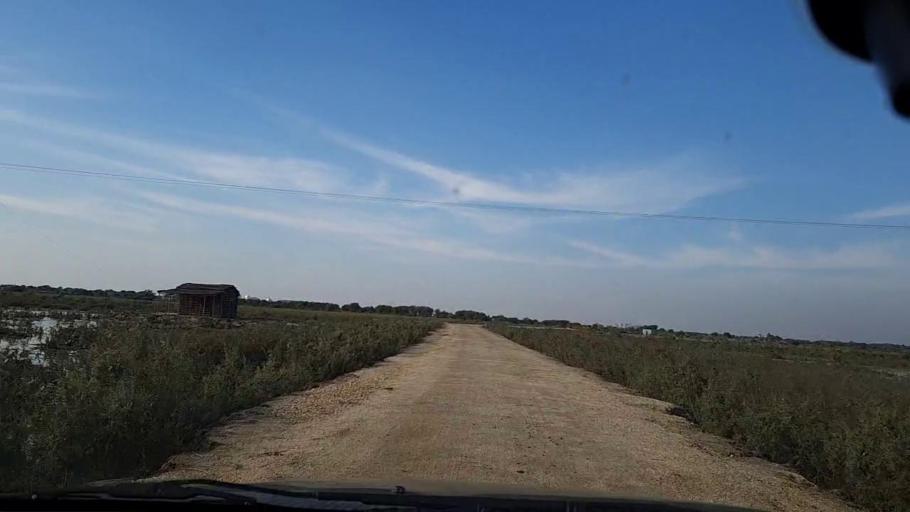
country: PK
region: Sindh
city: Mirpur Batoro
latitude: 24.6338
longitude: 68.2989
